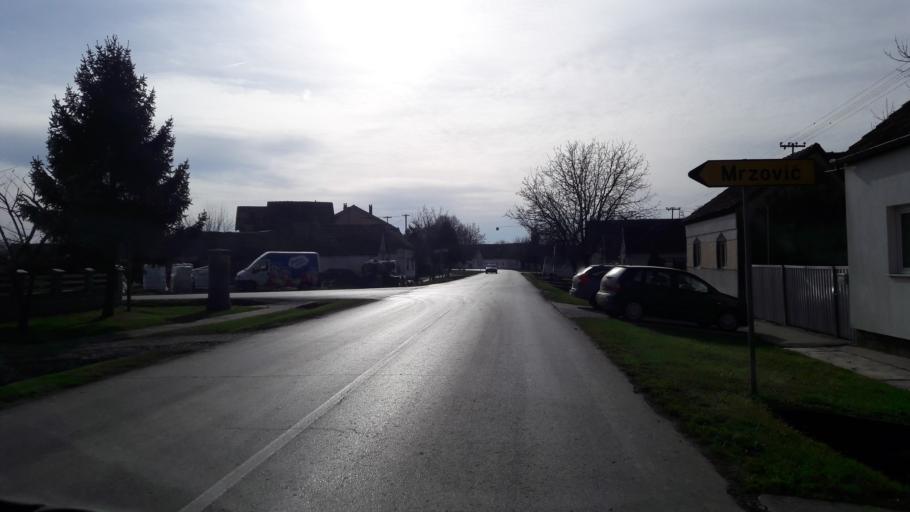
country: HR
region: Osjecko-Baranjska
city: Semeljci
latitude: 45.3101
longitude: 18.5572
